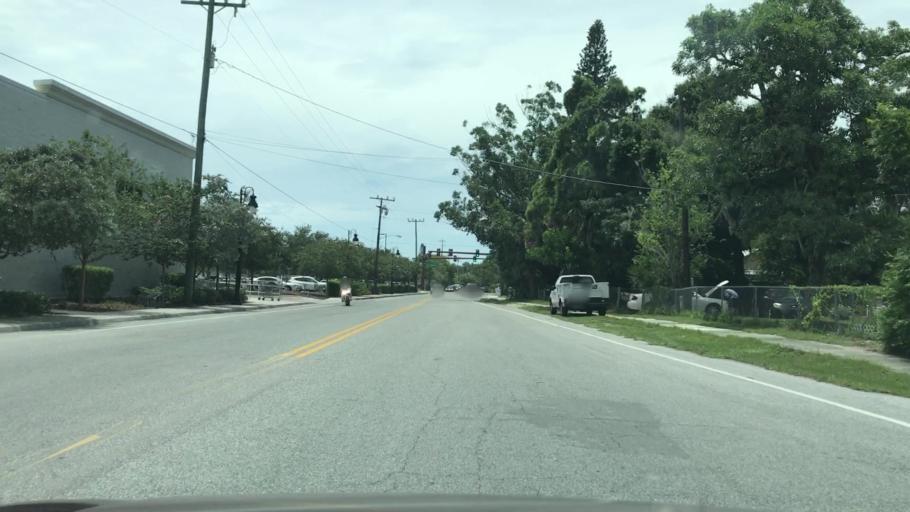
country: US
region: Florida
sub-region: Sarasota County
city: North Sarasota
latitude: 27.3672
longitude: -82.5500
